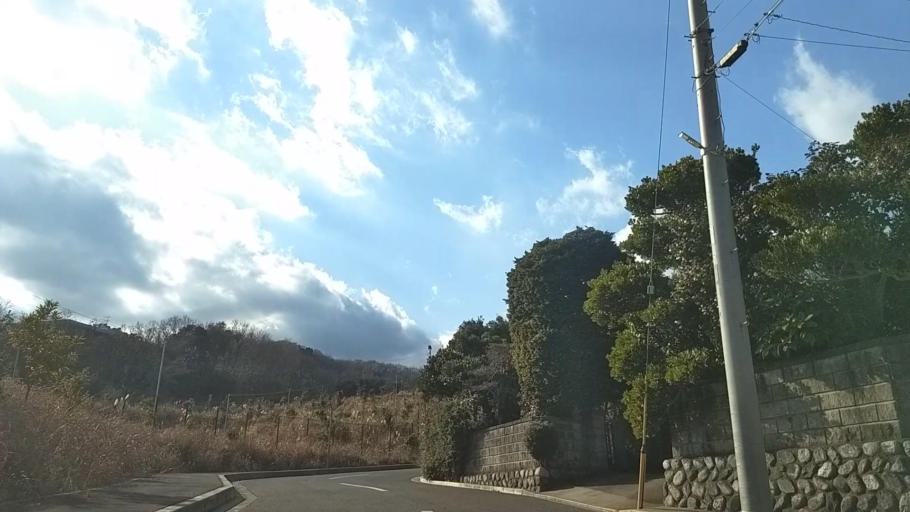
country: JP
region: Kanagawa
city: Isehara
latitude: 35.4267
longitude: 139.3153
